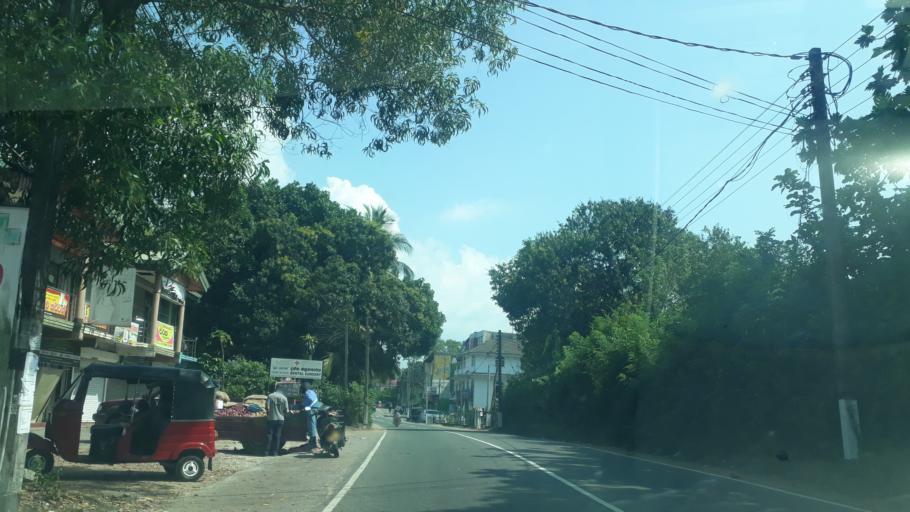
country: LK
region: Western
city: Gampaha
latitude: 7.0752
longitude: 80.0145
